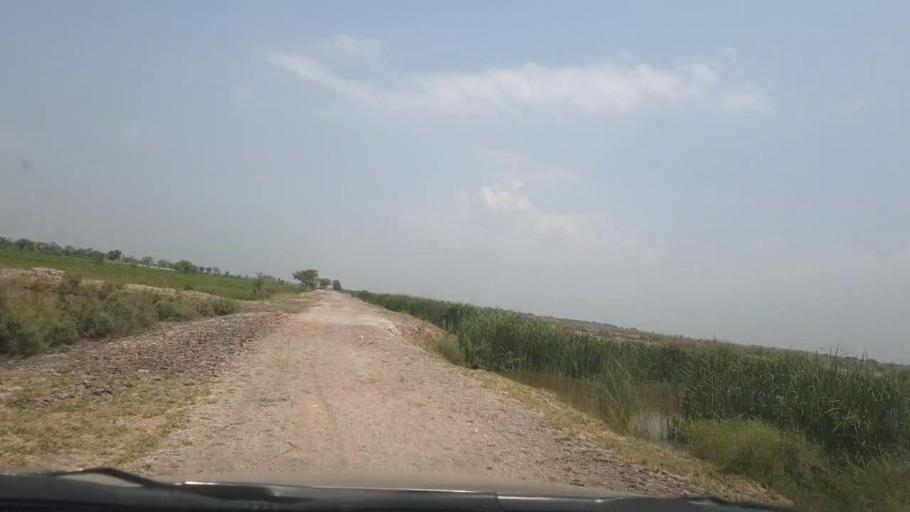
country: PK
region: Sindh
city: Naudero
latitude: 27.7193
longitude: 68.3011
